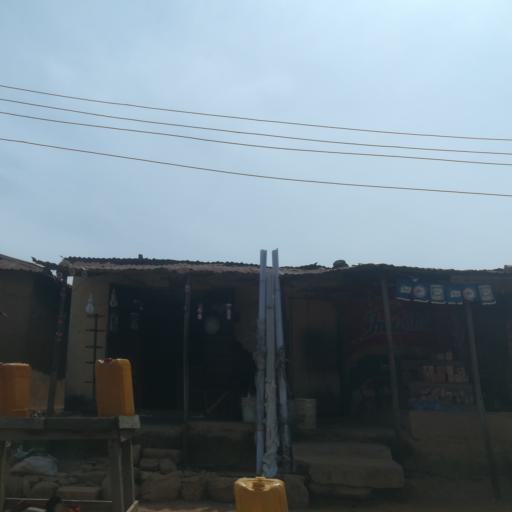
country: NG
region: Plateau
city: Jos
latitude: 9.9057
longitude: 8.8743
